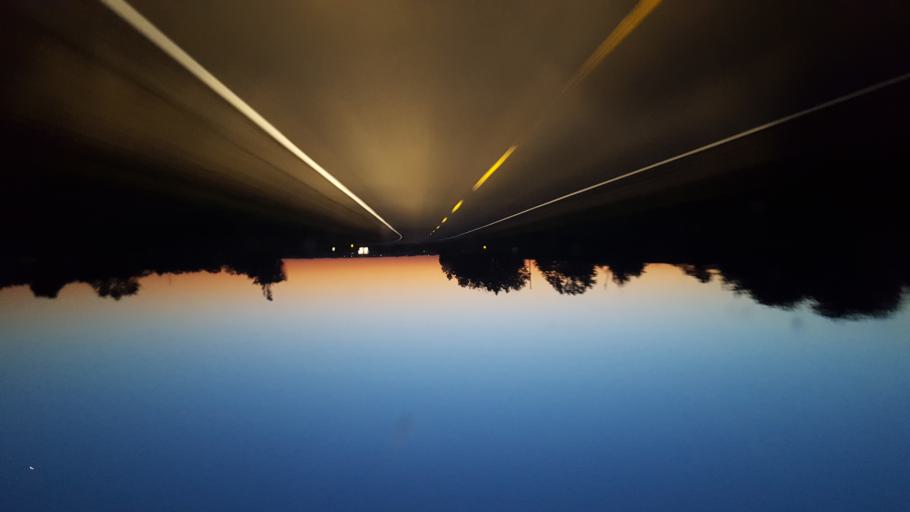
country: US
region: Missouri
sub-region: Mercer County
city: Princeton
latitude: 40.4016
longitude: -93.6346
